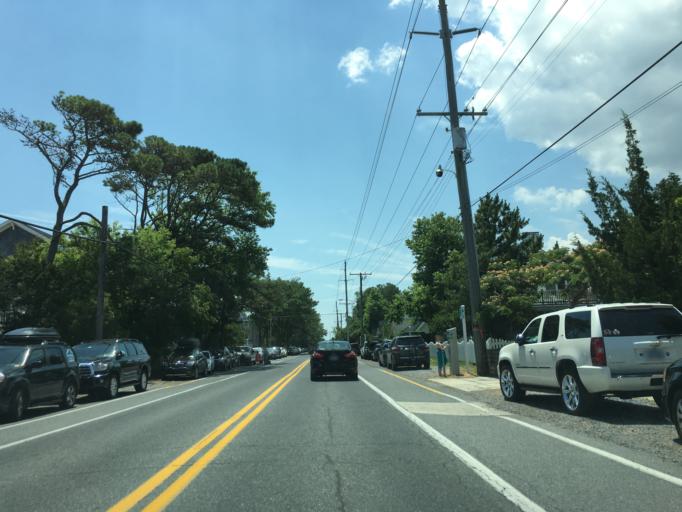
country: US
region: Delaware
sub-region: Sussex County
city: Bethany Beach
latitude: 38.5372
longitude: -75.0572
